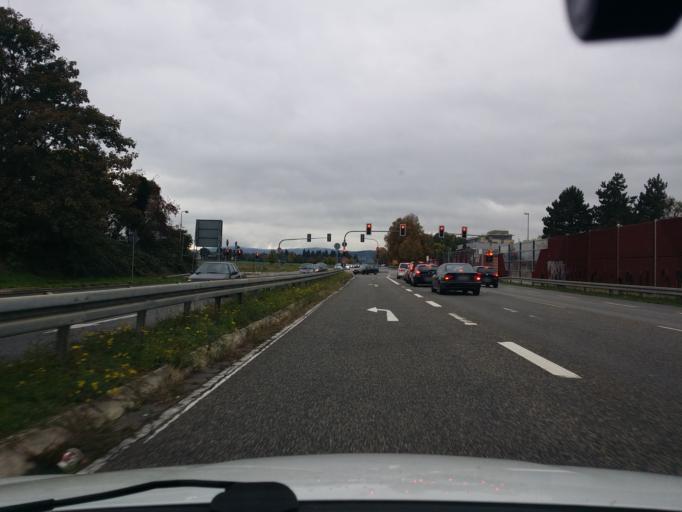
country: DE
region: Hesse
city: Sulzbach
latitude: 50.1255
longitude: 8.5218
